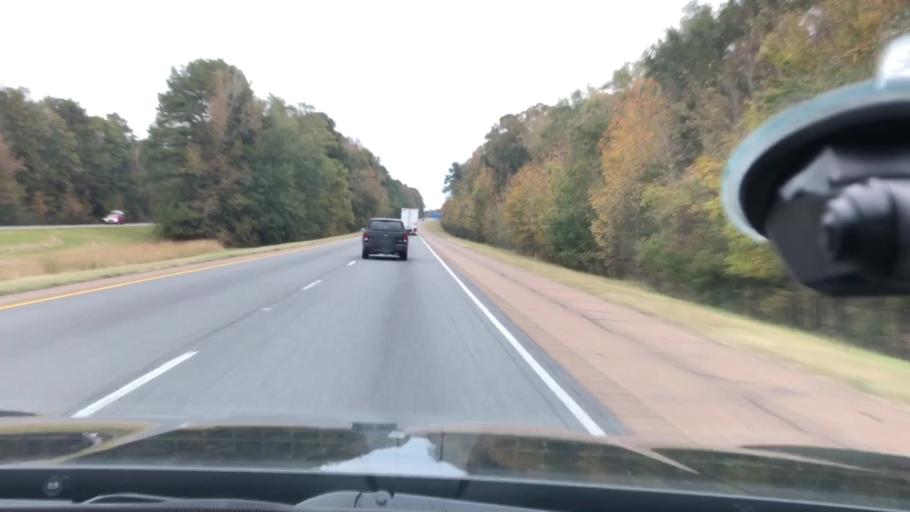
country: US
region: Arkansas
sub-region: Clark County
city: Gurdon
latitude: 33.9166
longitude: -93.2786
